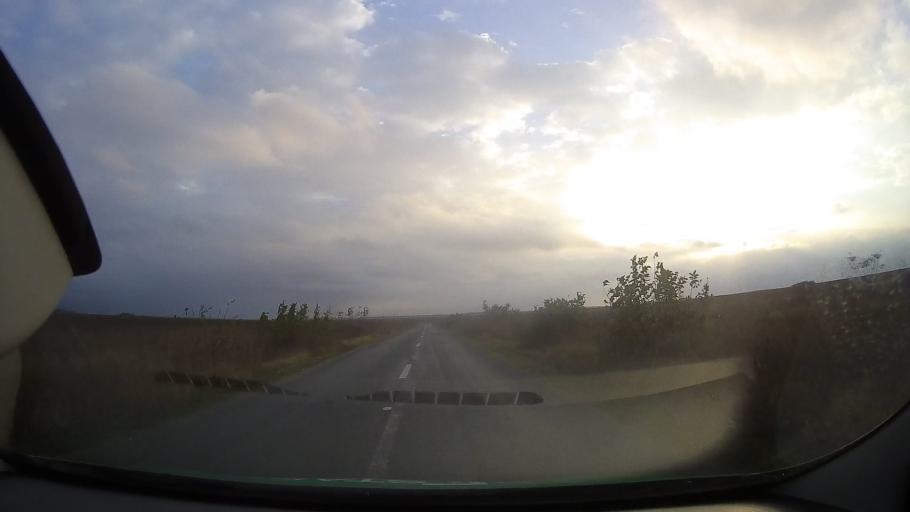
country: RO
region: Constanta
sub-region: Comuna Adamclisi
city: Adamclisi
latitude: 44.0215
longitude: 27.9070
